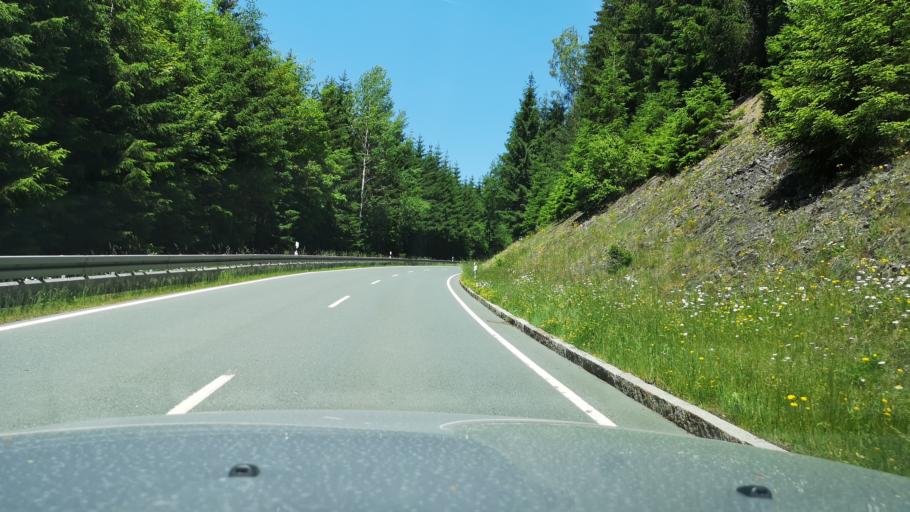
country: DE
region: Bavaria
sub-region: Upper Franconia
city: Tschirn
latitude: 50.4025
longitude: 11.4666
